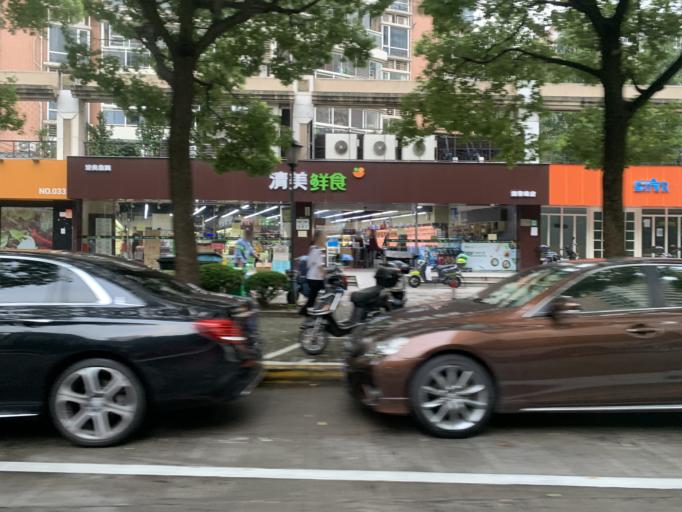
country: CN
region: Shanghai Shi
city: Huamu
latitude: 31.2259
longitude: 121.5495
